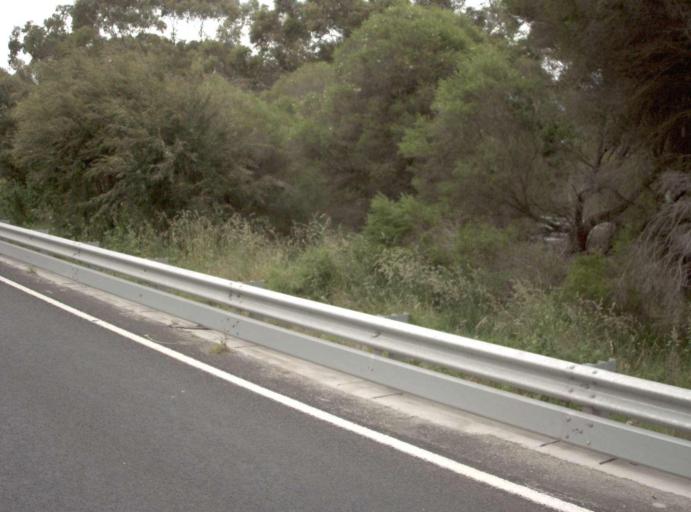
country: AU
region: Victoria
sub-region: Cardinia
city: Koo-Wee-Rup
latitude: -38.2899
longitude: 145.5460
